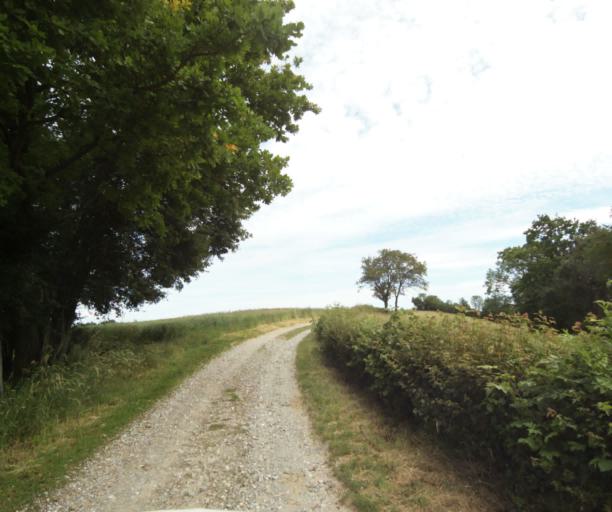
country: FR
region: Rhone-Alpes
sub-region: Departement de la Haute-Savoie
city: Margencel
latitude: 46.3408
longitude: 6.4257
